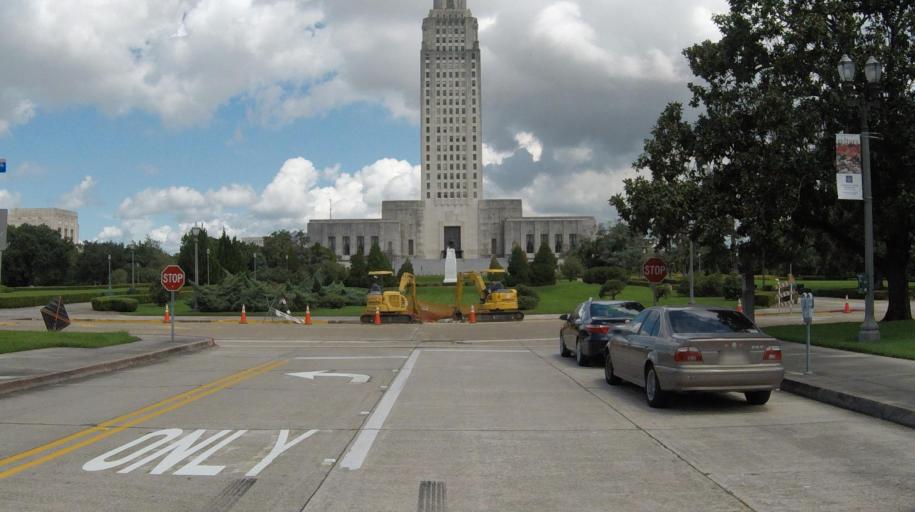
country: US
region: Louisiana
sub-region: West Baton Rouge Parish
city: Port Allen
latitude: 30.4543
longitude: -91.1873
